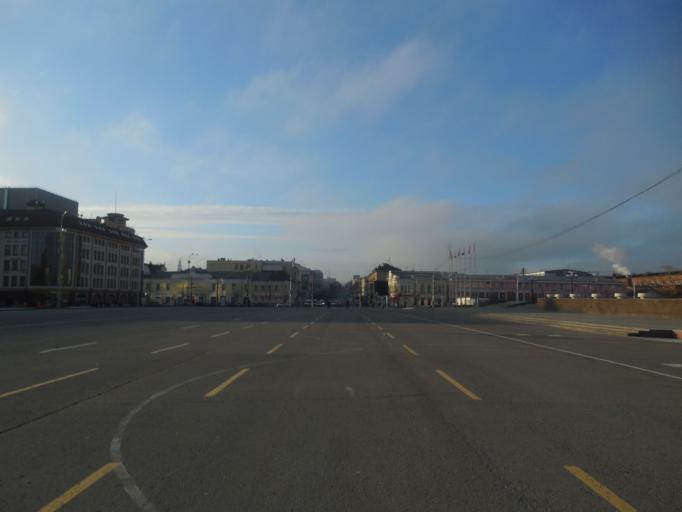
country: RU
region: Tula
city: Tula
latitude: 54.1935
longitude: 37.6179
